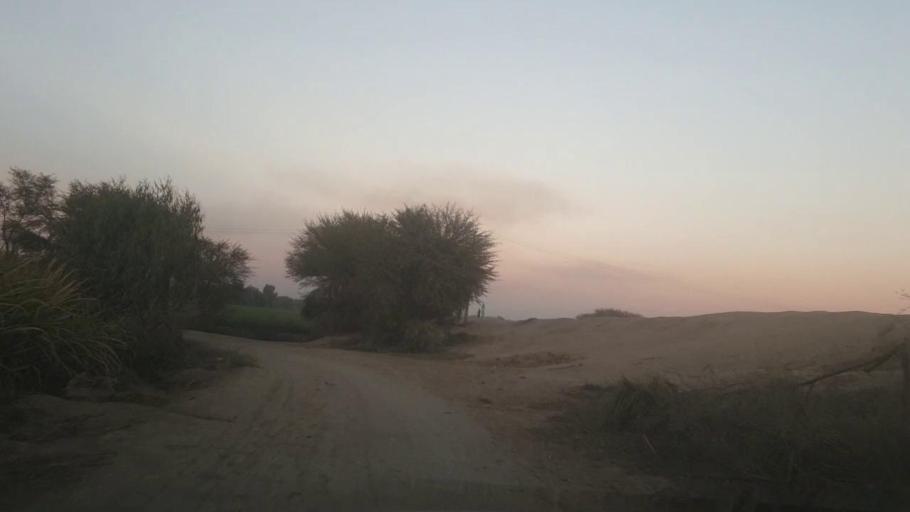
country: PK
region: Sindh
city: Ghotki
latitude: 28.0673
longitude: 69.3082
